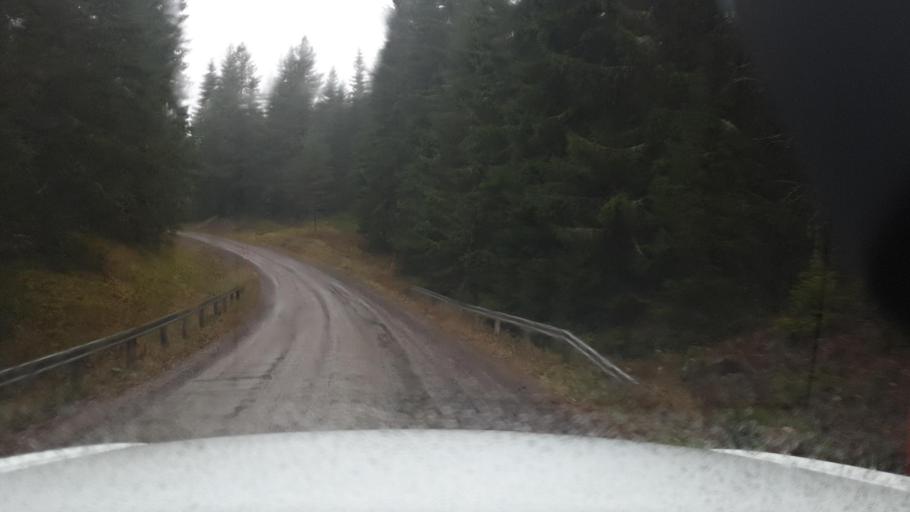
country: SE
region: Vaermland
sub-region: Sunne Kommun
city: Sunne
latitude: 59.8619
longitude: 12.8733
